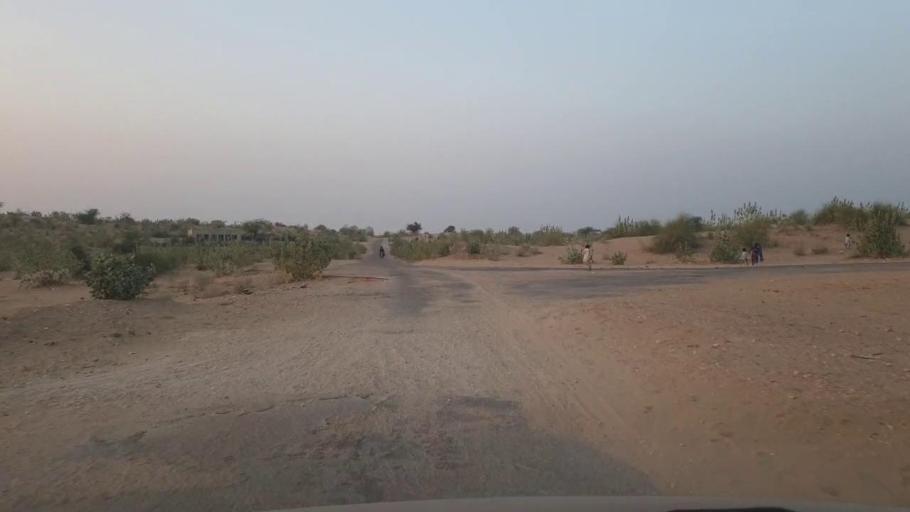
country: PK
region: Sindh
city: Umarkot
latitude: 25.2903
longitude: 70.0777
